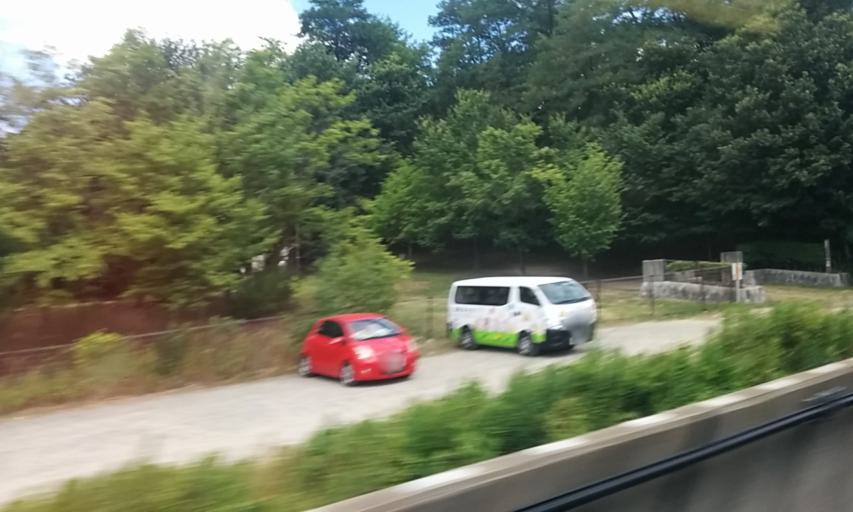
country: JP
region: Fukushima
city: Koriyama
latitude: 37.4315
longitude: 140.3991
